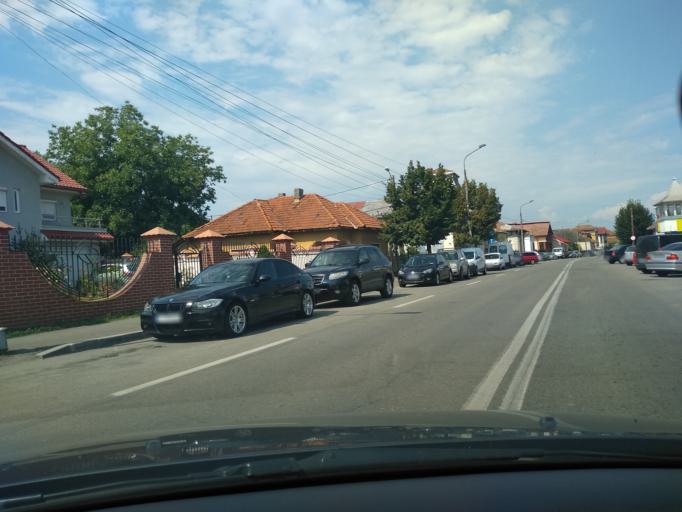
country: RO
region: Gorj
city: Targu Jiu
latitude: 45.0462
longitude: 23.2728
